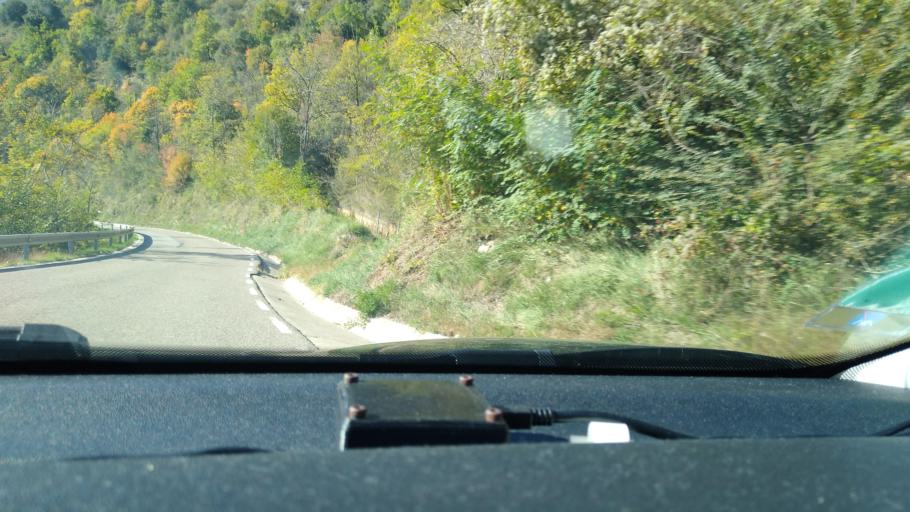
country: ES
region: Catalonia
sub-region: Provincia de Barcelona
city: Vallcebre
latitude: 42.1794
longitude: 1.8609
